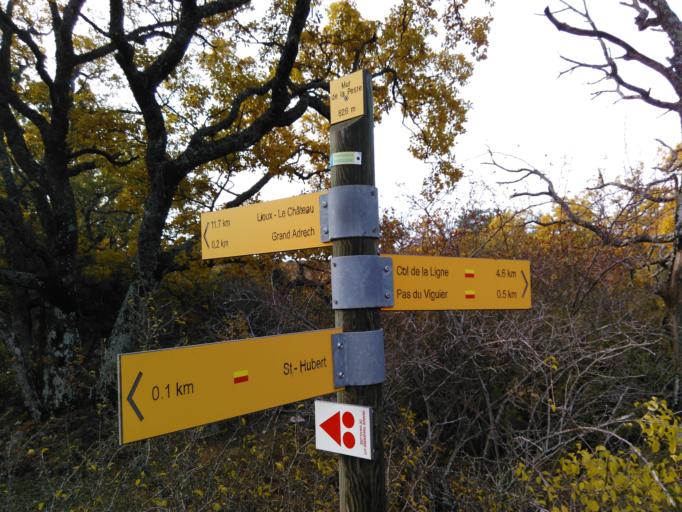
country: FR
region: Provence-Alpes-Cote d'Azur
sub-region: Departement du Vaucluse
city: Villes-sur-Auzon
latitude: 44.0259
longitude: 5.3193
